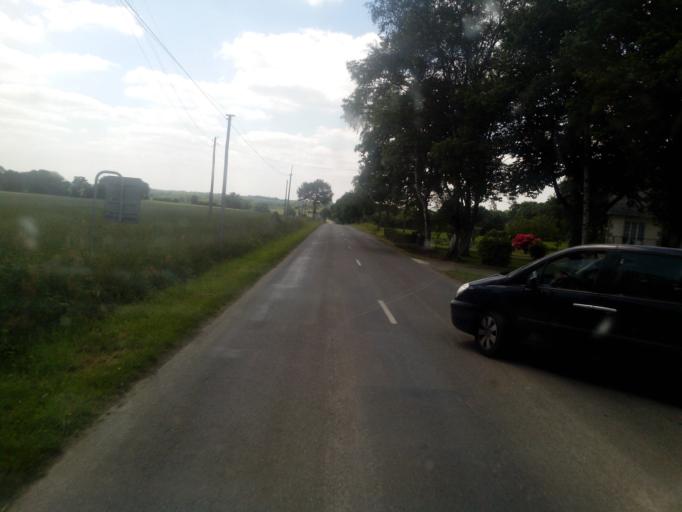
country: FR
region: Brittany
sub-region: Departement d'Ille-et-Vilaine
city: Sens-de-Bretagne
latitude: 48.3278
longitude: -1.5706
